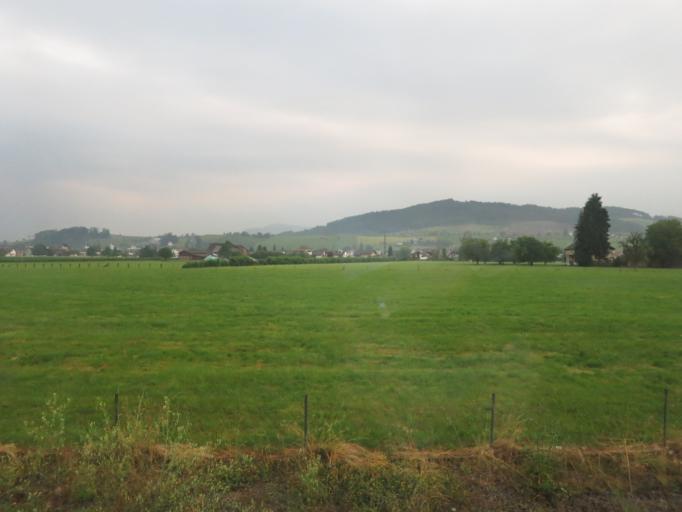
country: CH
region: Schwyz
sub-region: Bezirk March
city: Schubelbach
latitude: 47.1830
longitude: 8.9018
